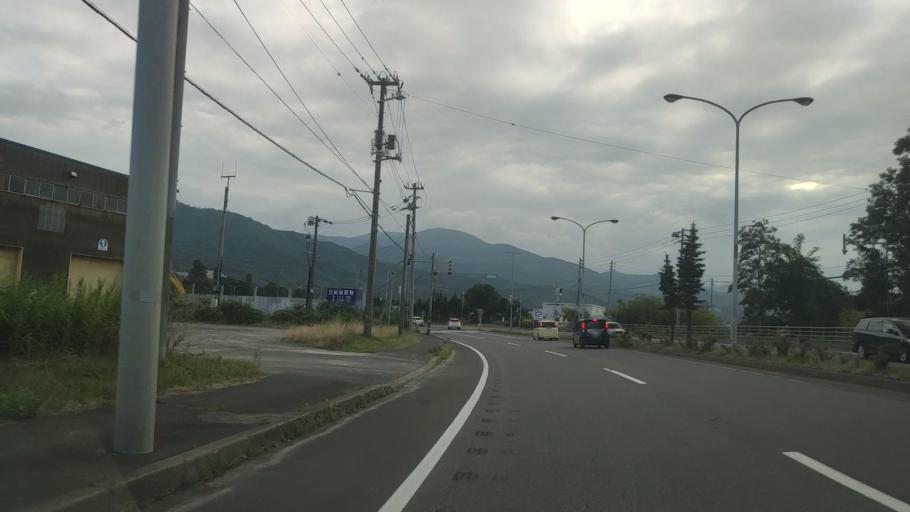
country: JP
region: Hokkaido
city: Sapporo
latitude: 43.1441
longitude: 141.1817
